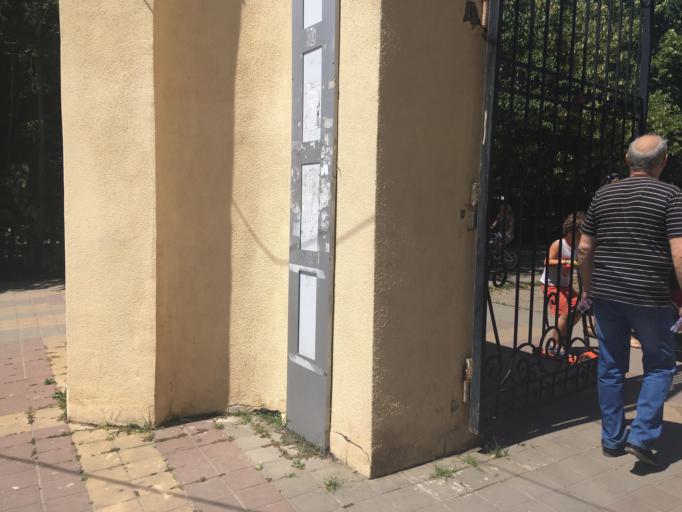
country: RU
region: Rostov
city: Rostov-na-Donu
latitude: 47.2095
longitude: 39.6337
